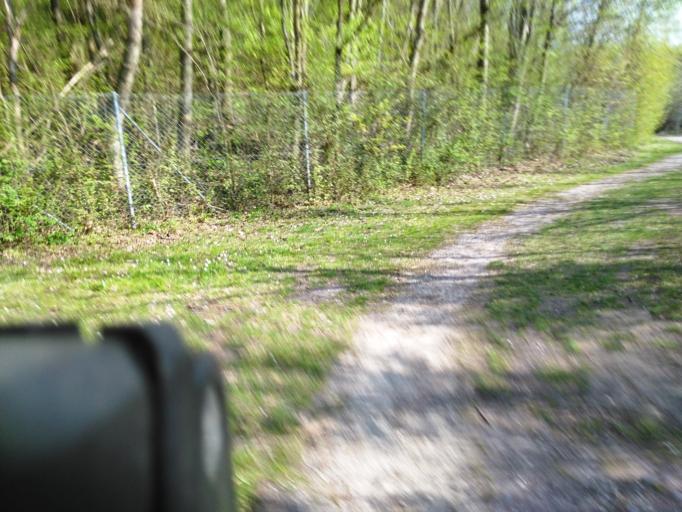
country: DE
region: Bavaria
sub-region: Upper Bavaria
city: Mammendorf
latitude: 48.2006
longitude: 11.1698
